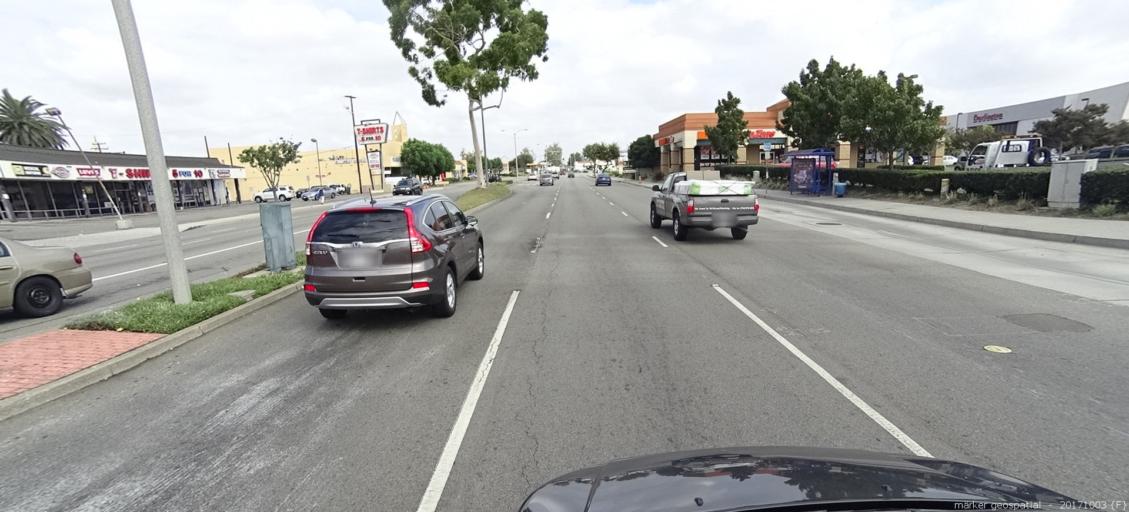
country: US
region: California
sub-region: Orange County
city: Garden Grove
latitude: 33.7718
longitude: -117.9203
